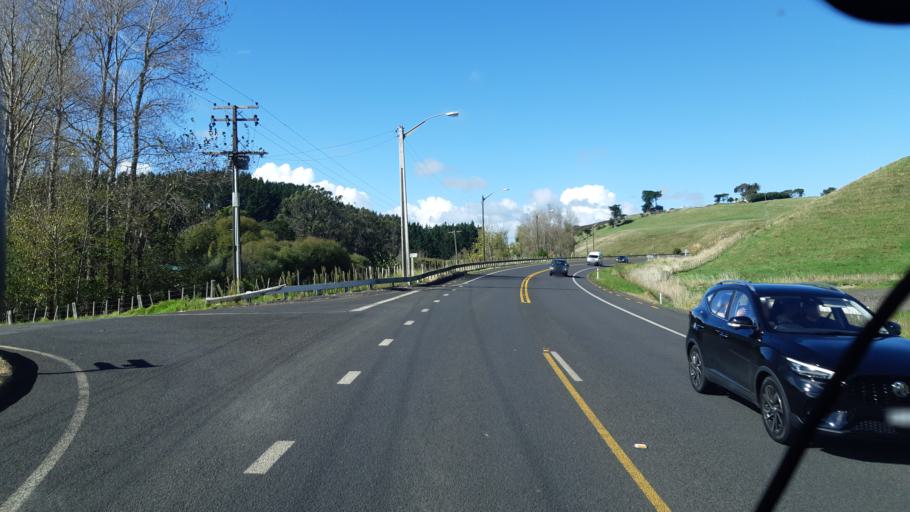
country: NZ
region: Manawatu-Wanganui
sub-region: Wanganui District
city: Wanganui
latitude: -39.9609
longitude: 175.0974
